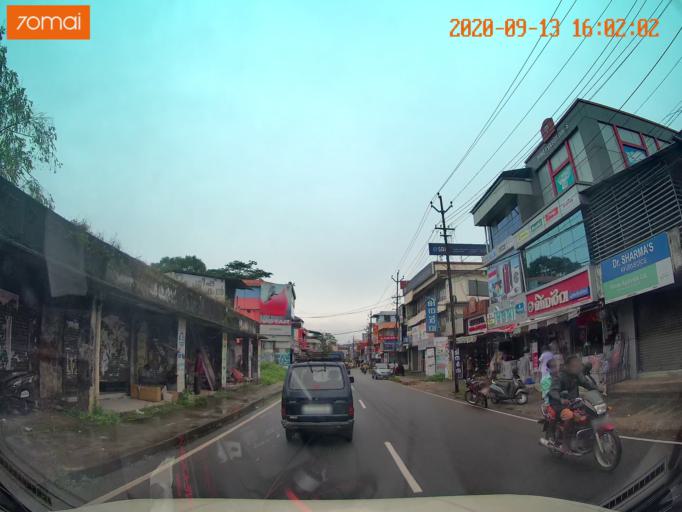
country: IN
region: Kerala
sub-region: Kottayam
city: Kottayam
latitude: 9.6708
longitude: 76.5593
